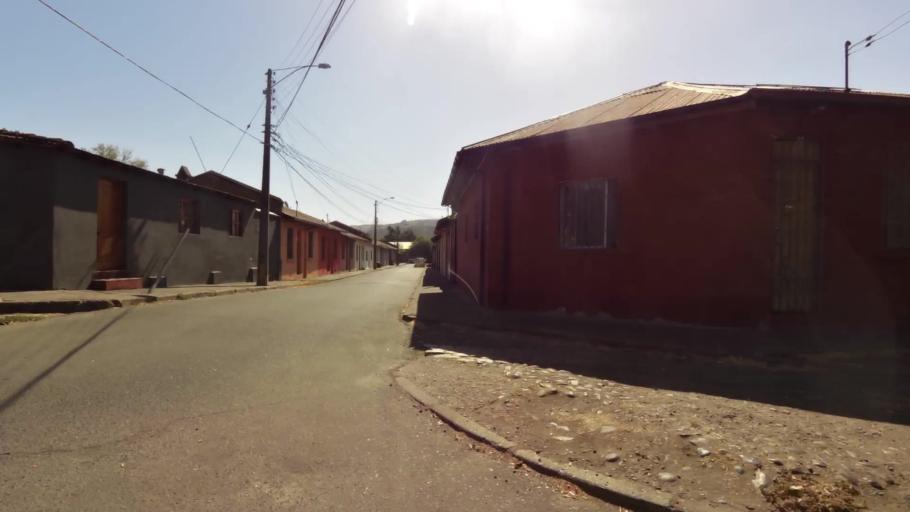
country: CL
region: Maule
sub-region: Provincia de Talca
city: Talca
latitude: -35.4177
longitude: -71.6631
